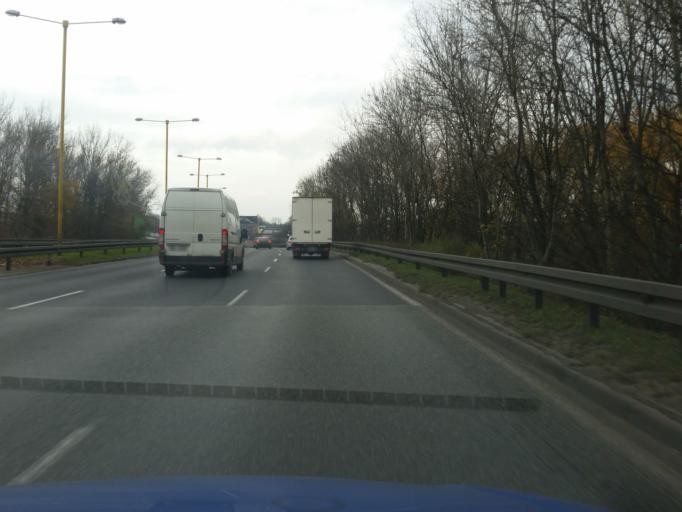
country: PL
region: Silesian Voivodeship
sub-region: Czestochowa
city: Czestochowa
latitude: 50.8009
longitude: 19.1335
